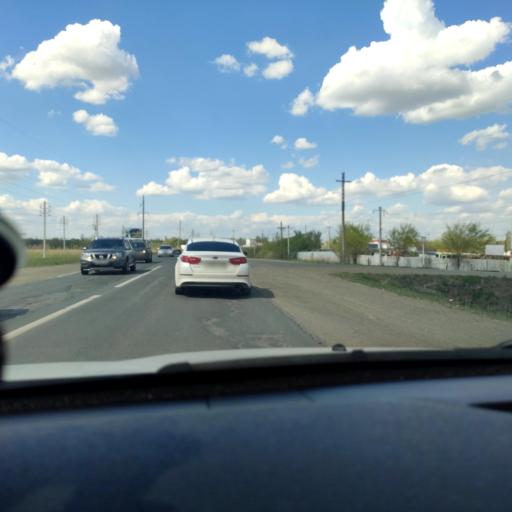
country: RU
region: Samara
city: Kinel'
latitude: 53.2357
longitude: 50.5828
